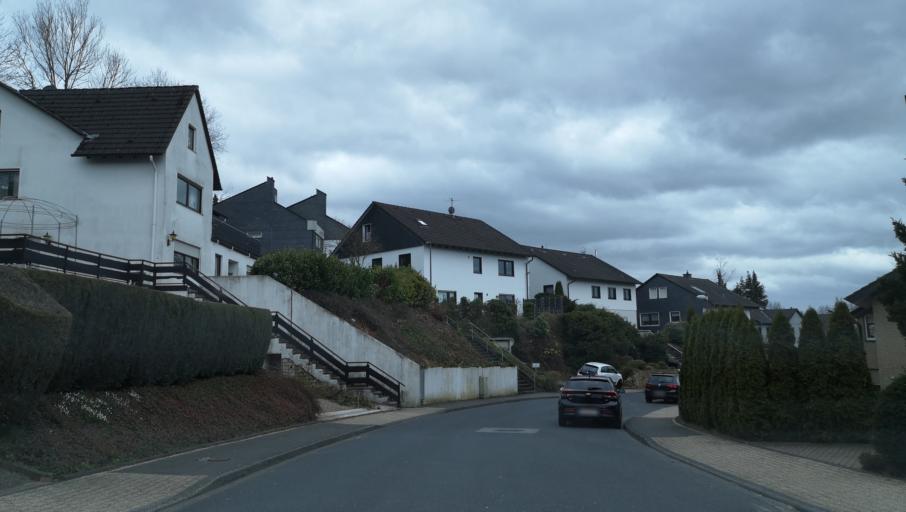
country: DE
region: North Rhine-Westphalia
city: Radevormwald
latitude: 51.2168
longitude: 7.3157
